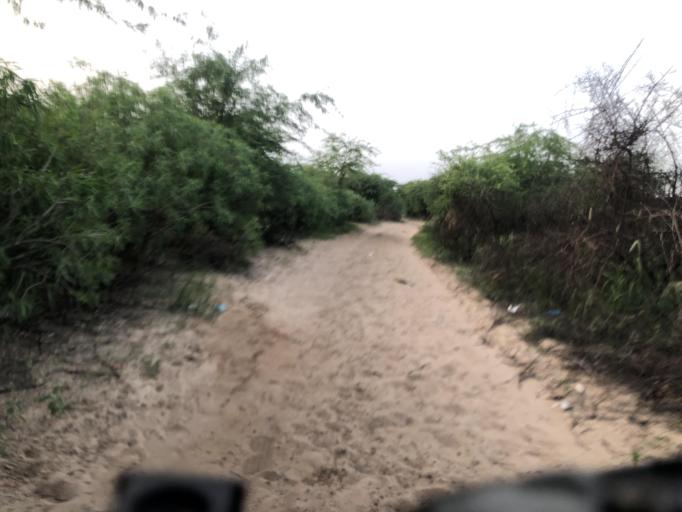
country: SN
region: Saint-Louis
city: Saint-Louis
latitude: 16.0580
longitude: -16.4319
